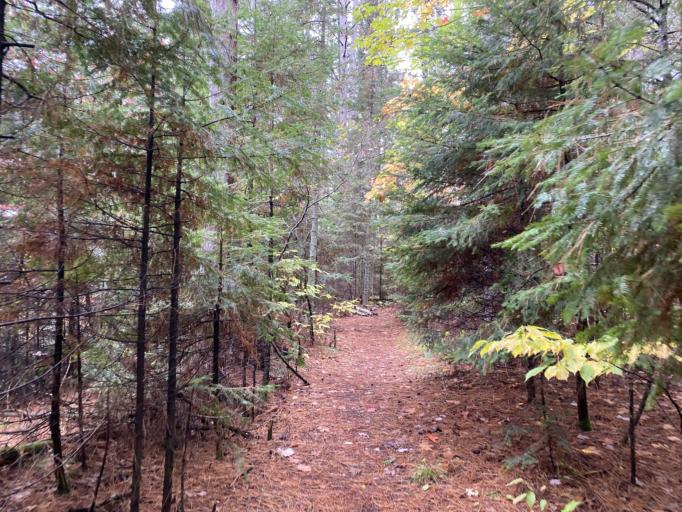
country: US
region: Michigan
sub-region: Marquette County
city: West Ishpeming
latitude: 46.5328
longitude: -88.0009
